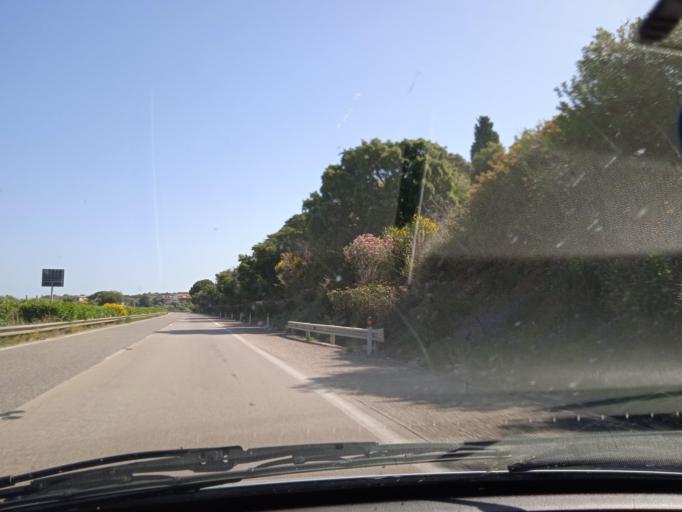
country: IT
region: Sicily
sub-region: Messina
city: Rocca di Capri Leone
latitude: 38.1134
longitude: 14.7245
